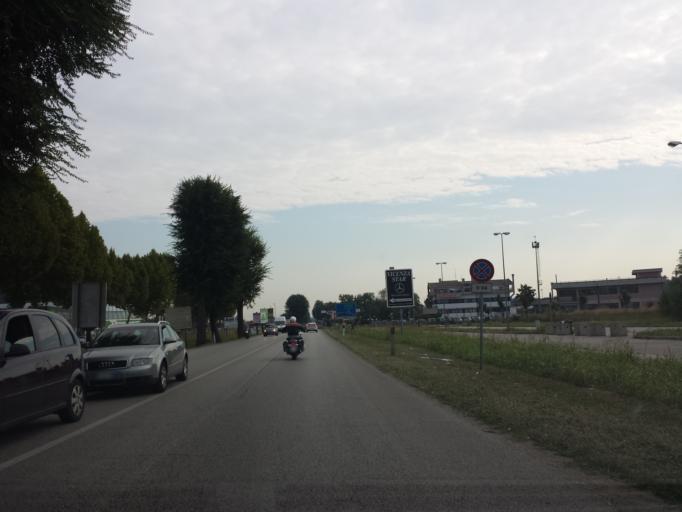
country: IT
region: Veneto
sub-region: Provincia di Vicenza
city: Altavilla Vicentina
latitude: 45.5164
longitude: 11.4651
